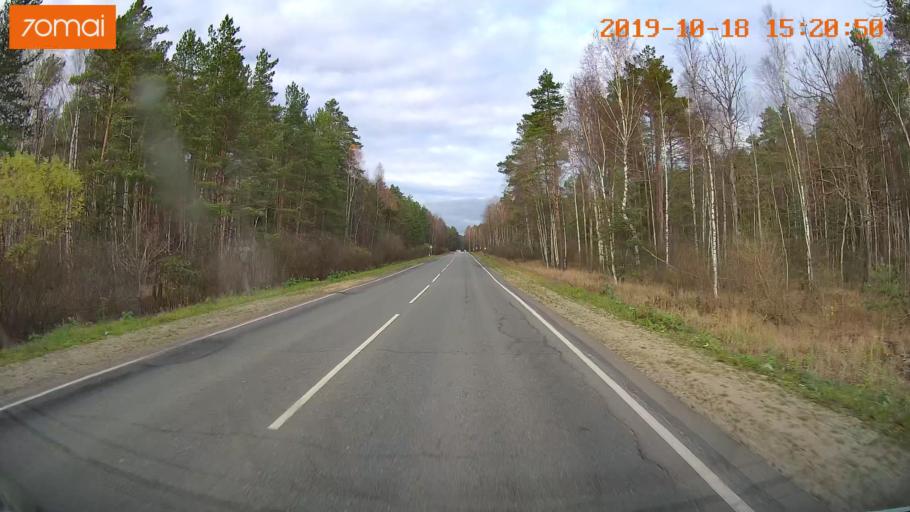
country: RU
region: Vladimir
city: Anopino
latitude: 55.6913
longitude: 40.7473
